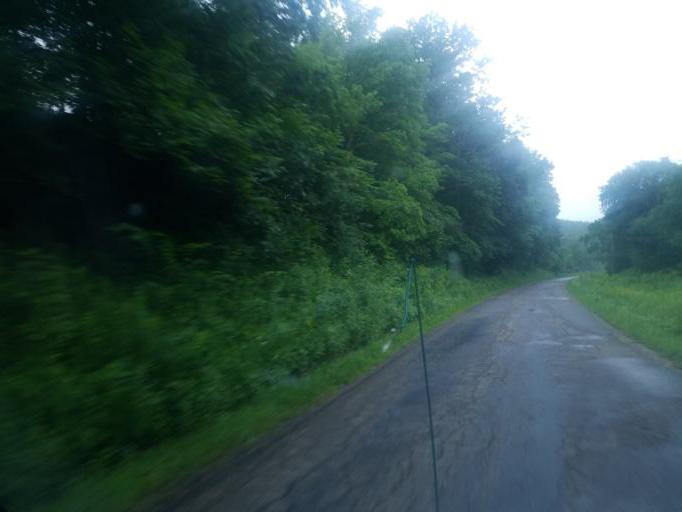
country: US
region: Ohio
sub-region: Columbiana County
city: Salineville
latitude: 40.6034
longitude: -80.9230
